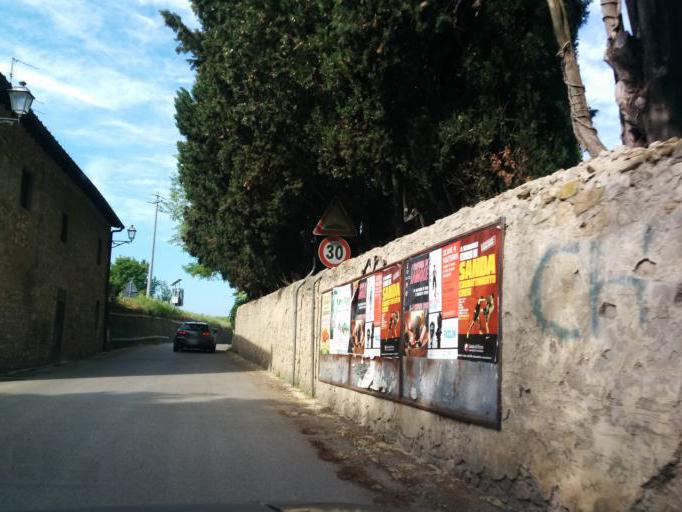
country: IT
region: Tuscany
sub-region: Province of Florence
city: San Casciano in Val di Pesa
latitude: 43.6825
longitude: 11.1972
